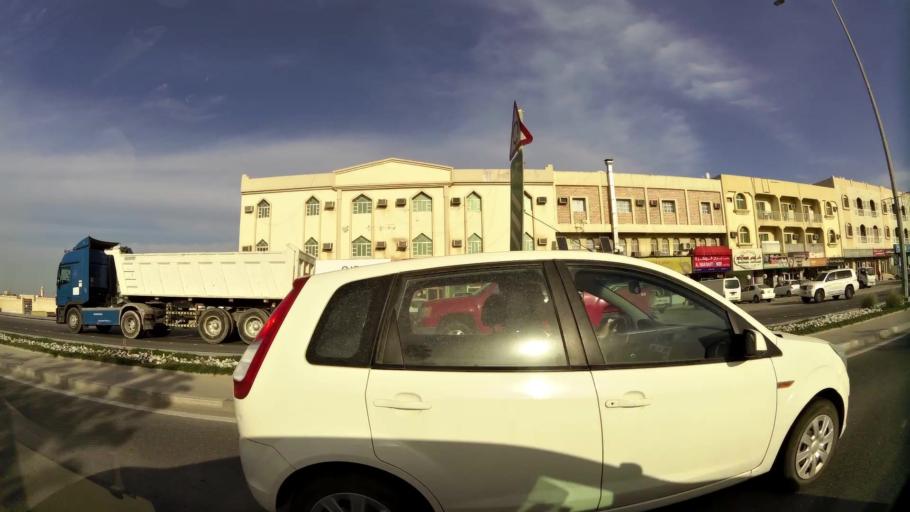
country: QA
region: Al Wakrah
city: Al Wakrah
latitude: 25.1643
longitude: 51.6076
